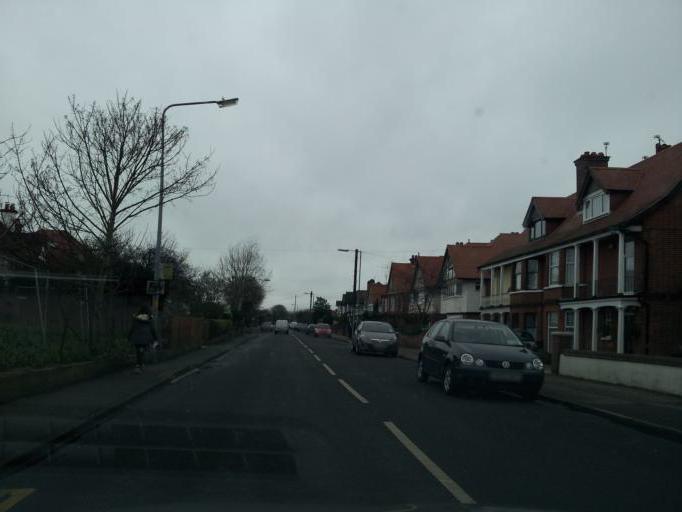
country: GB
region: England
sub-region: Essex
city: Dovercourt
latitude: 51.9321
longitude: 1.2719
